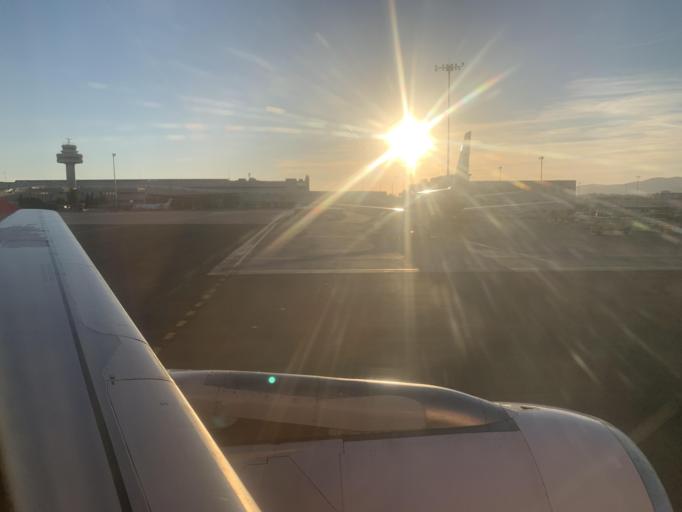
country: ES
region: Balearic Islands
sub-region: Illes Balears
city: s'Arenal
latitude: 39.5523
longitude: 2.7359
